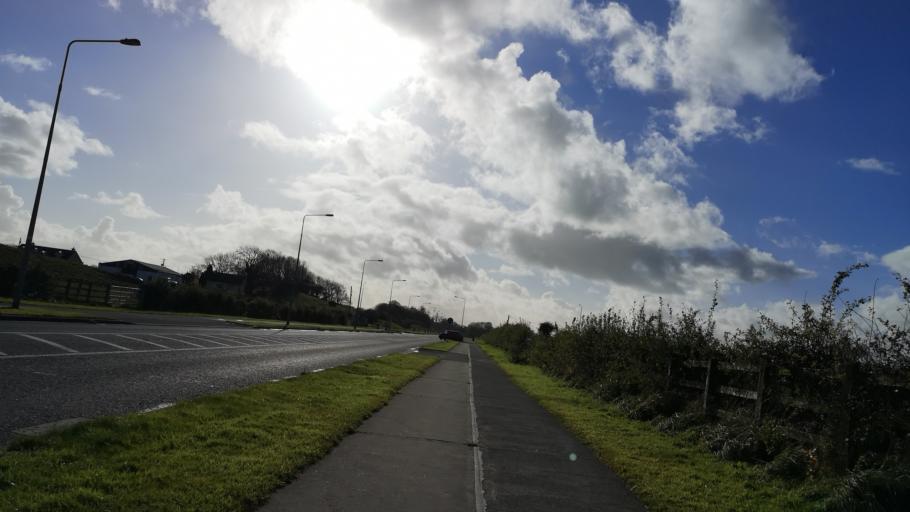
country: IE
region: Connaught
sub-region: County Galway
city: Athenry
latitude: 53.3079
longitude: -8.7605
